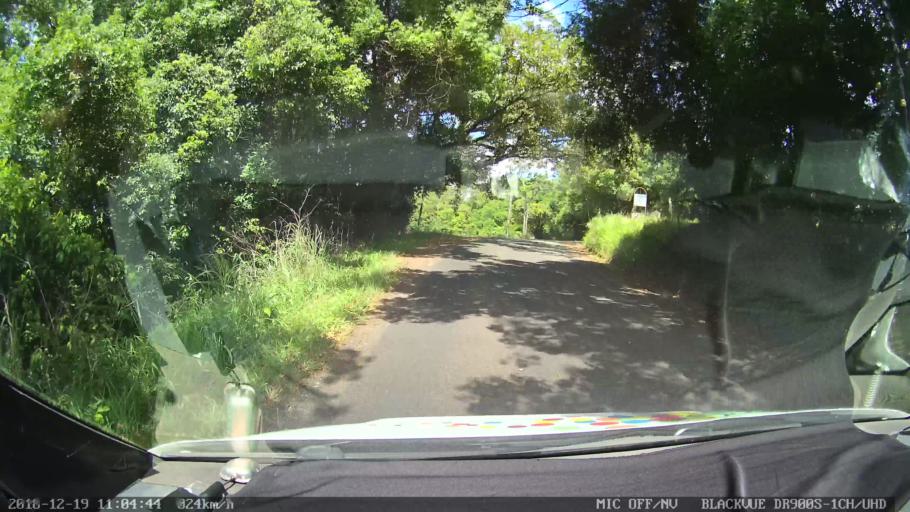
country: AU
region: New South Wales
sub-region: Lismore Municipality
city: Nimbin
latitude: -28.6153
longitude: 153.2669
